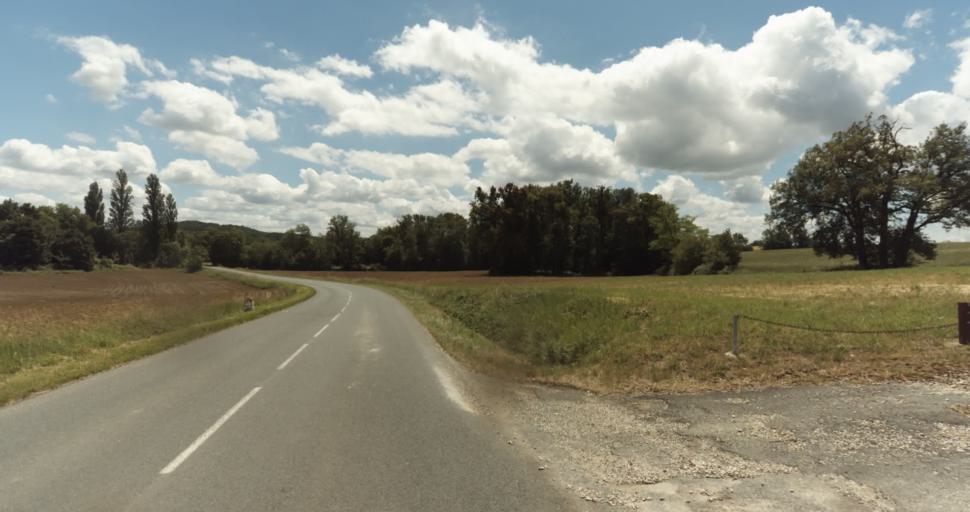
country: FR
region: Aquitaine
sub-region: Departement du Lot-et-Garonne
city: Villereal
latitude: 44.6810
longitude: 0.7606
